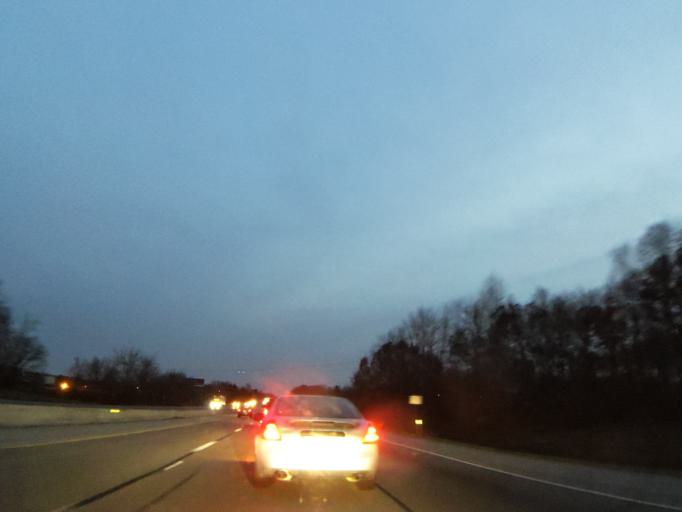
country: US
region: Kentucky
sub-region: Laurel County
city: London
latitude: 37.0951
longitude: -84.1007
